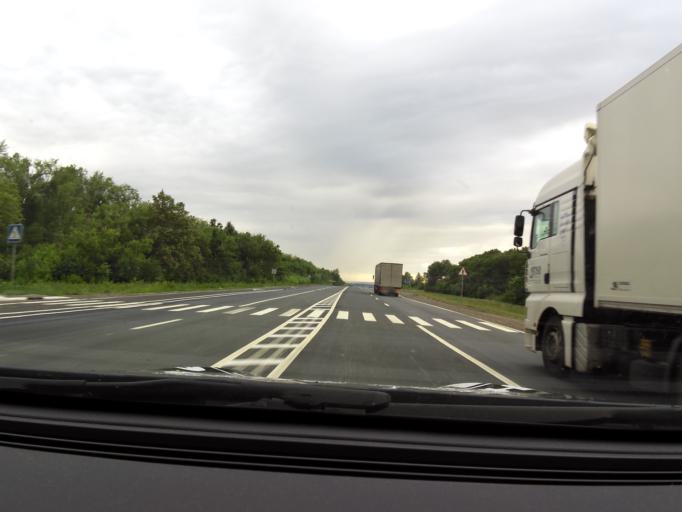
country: RU
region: Chuvashia
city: Yantikovo
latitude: 55.8092
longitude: 48.0289
